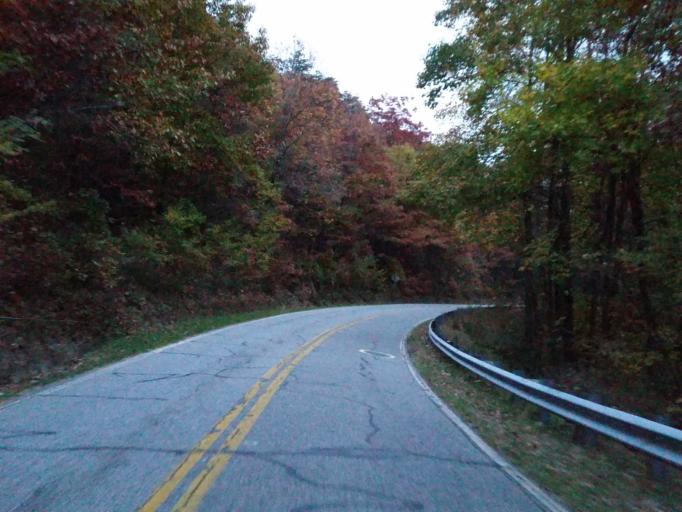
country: US
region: Georgia
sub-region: Lumpkin County
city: Dahlonega
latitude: 34.6731
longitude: -83.9899
